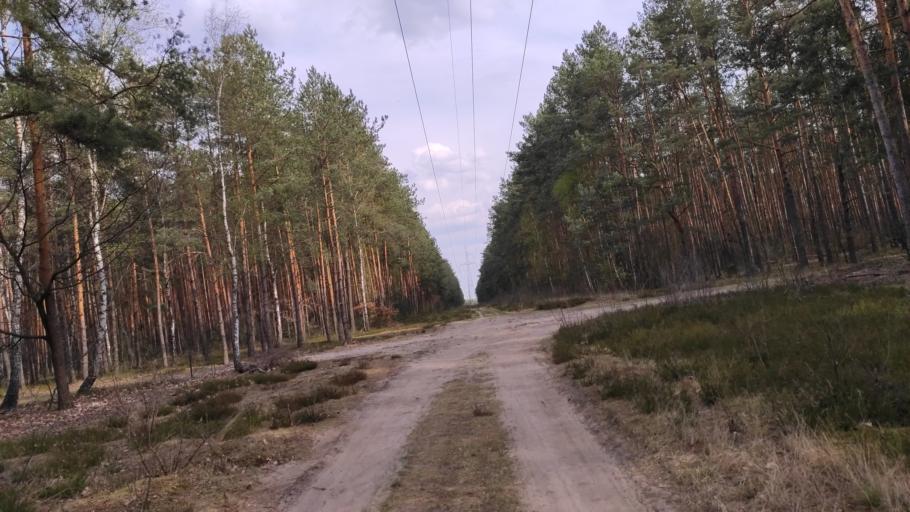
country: PL
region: Masovian Voivodeship
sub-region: Powiat grojecki
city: Warka
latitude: 51.7526
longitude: 21.1878
